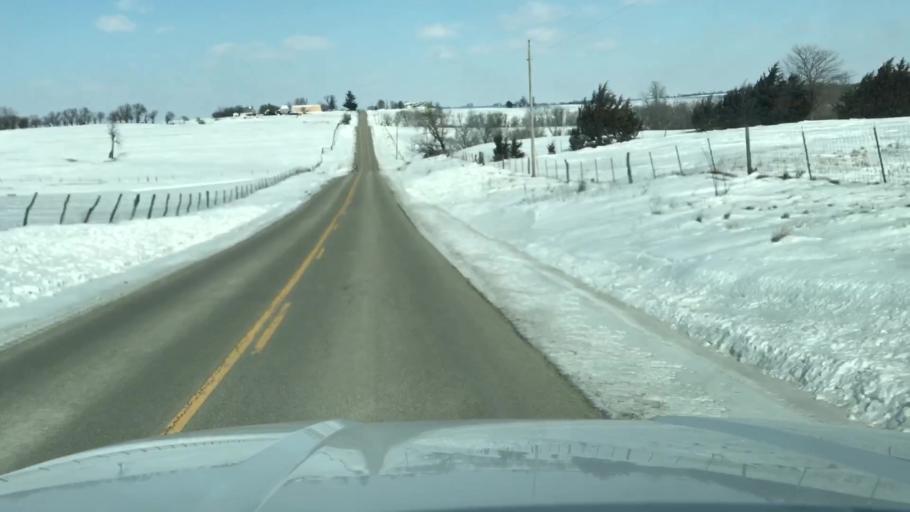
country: US
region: Missouri
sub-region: Nodaway County
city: Maryville
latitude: 40.3747
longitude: -94.7215
